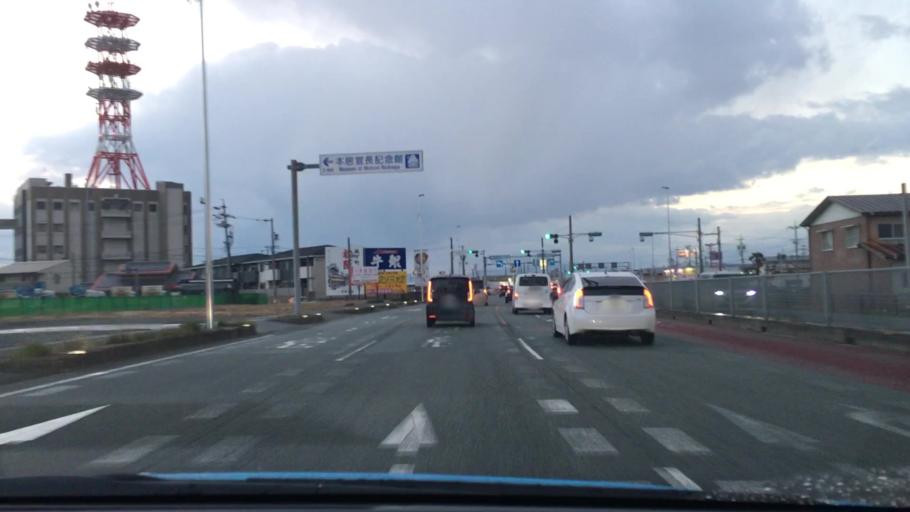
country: JP
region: Mie
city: Hisai-motomachi
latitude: 34.5894
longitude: 136.5472
